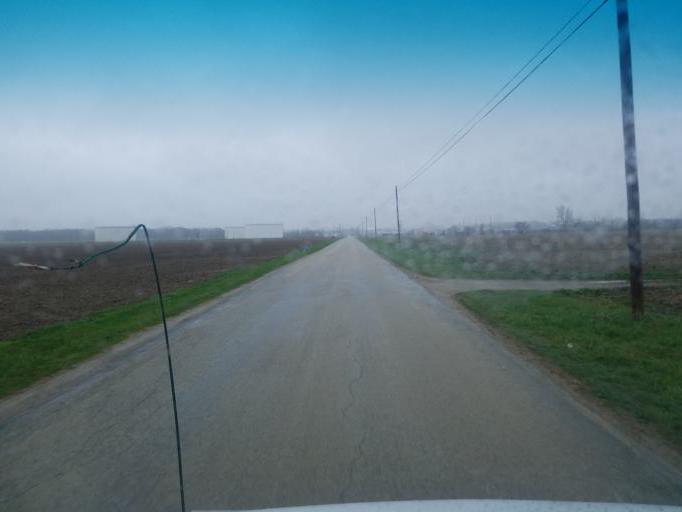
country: US
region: Ohio
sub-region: Wood County
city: North Baltimore
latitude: 41.2331
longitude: -83.6404
